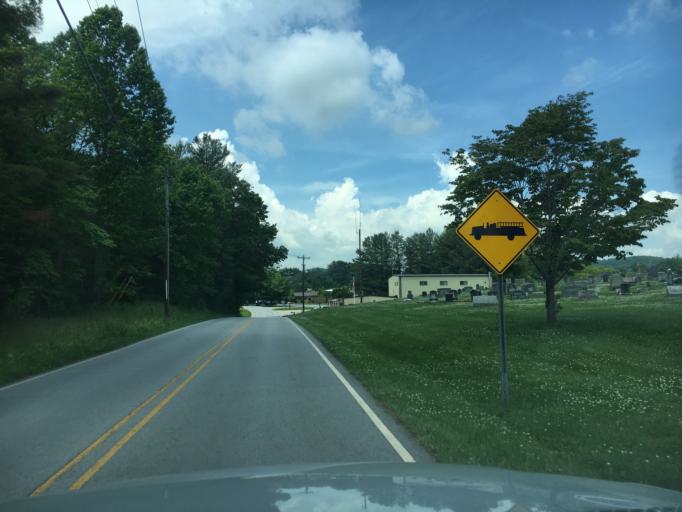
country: US
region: North Carolina
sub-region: Henderson County
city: Mills River
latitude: 35.3775
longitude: -82.5723
